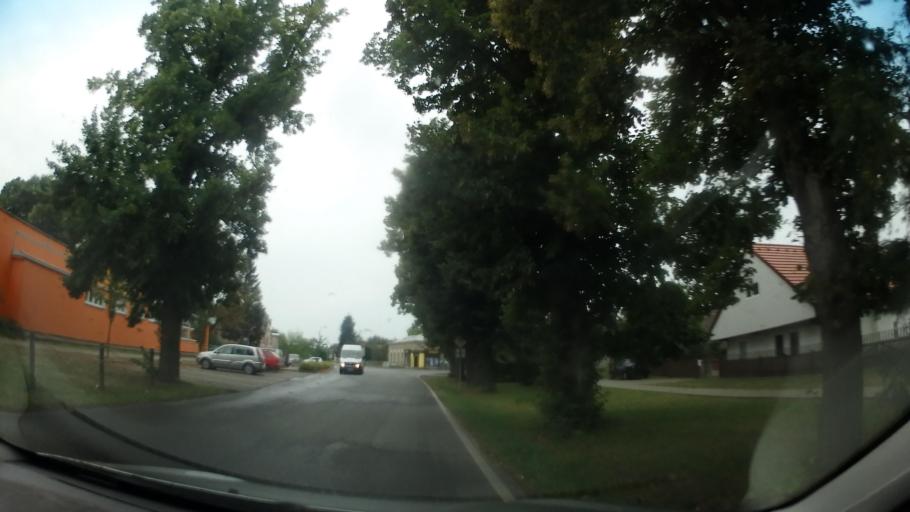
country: CZ
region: Central Bohemia
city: Loucen
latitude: 50.2866
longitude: 15.0210
